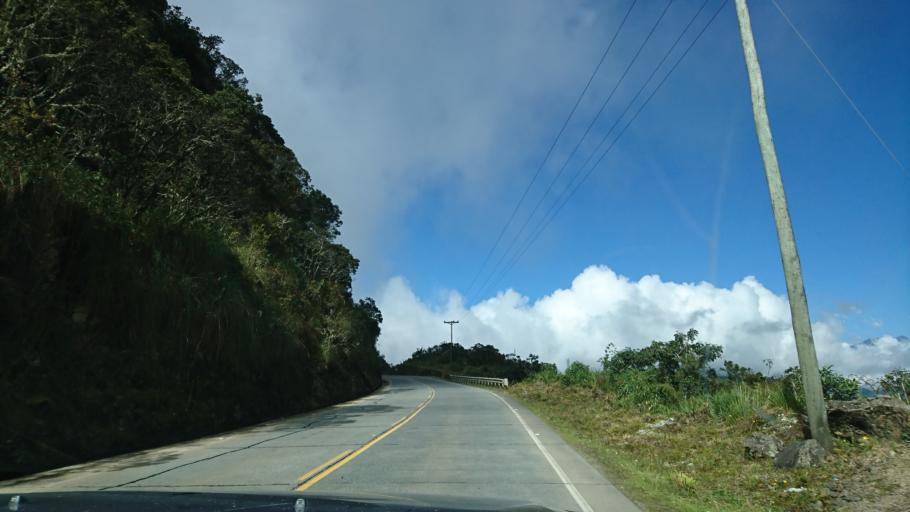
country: BO
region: La Paz
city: Coroico
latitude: -16.2863
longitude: -67.8387
